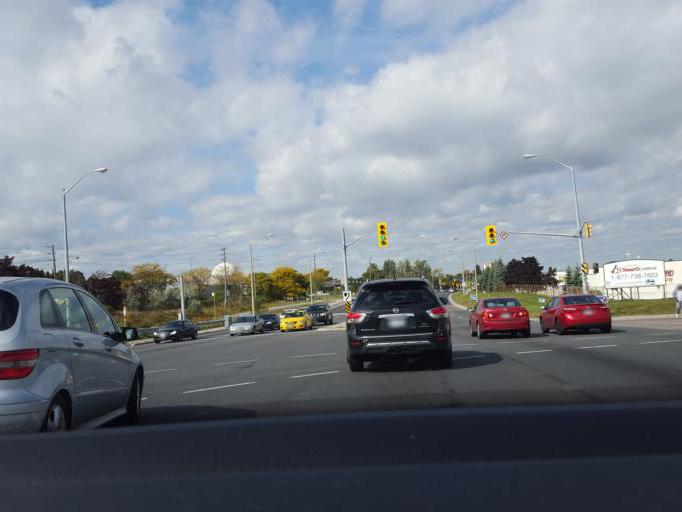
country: CA
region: Ontario
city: Scarborough
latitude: 43.7978
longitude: -79.1976
